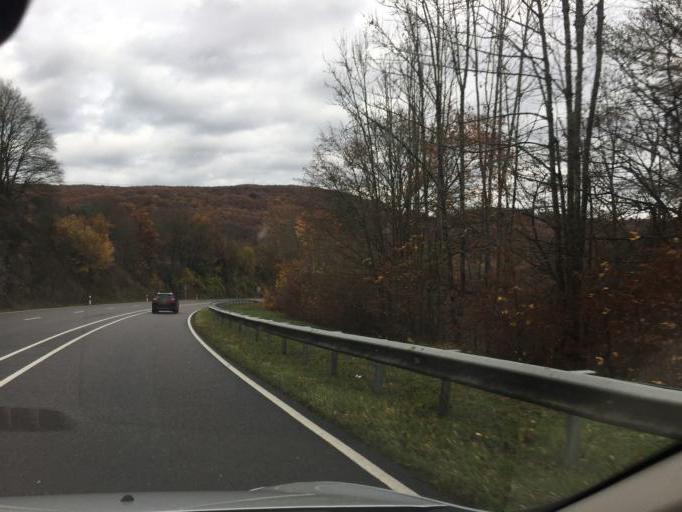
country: LU
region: Diekirch
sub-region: Canton de Wiltz
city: Goesdorf
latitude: 49.9014
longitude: 5.9591
